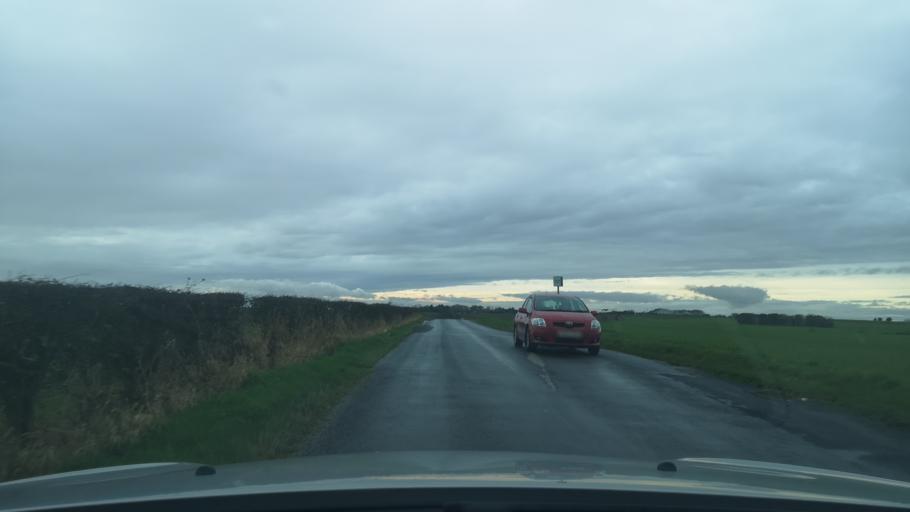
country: GB
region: England
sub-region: East Riding of Yorkshire
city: Holmpton
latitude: 53.6780
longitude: 0.0838
